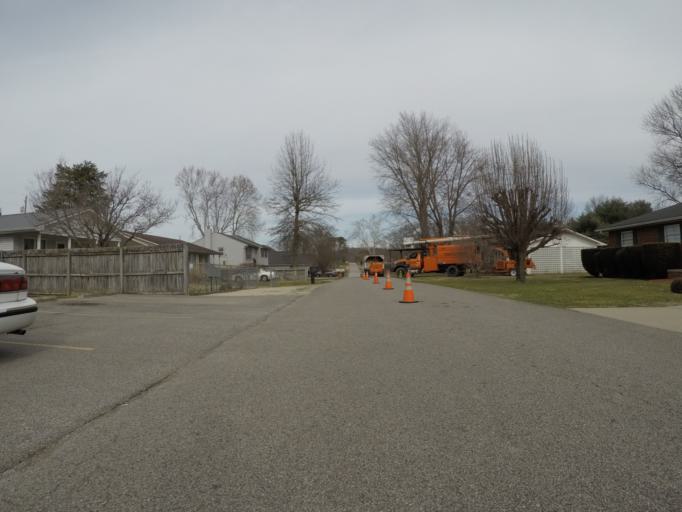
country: US
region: West Virginia
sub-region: Cabell County
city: Pea Ridge
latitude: 38.4465
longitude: -82.3475
